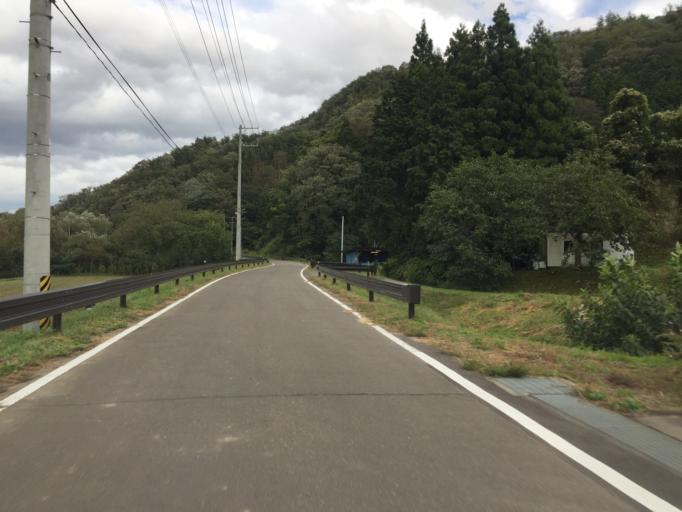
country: JP
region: Miyagi
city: Marumori
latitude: 37.9241
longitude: 140.7510
